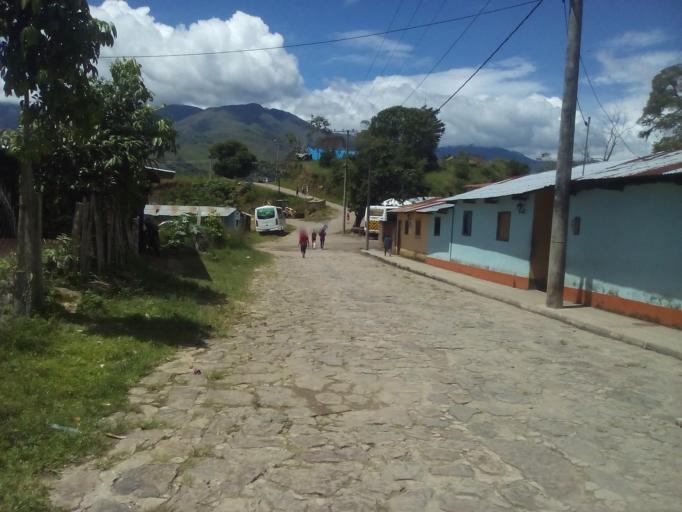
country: CO
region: Casanare
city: Nunchia
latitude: 5.6254
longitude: -72.4241
